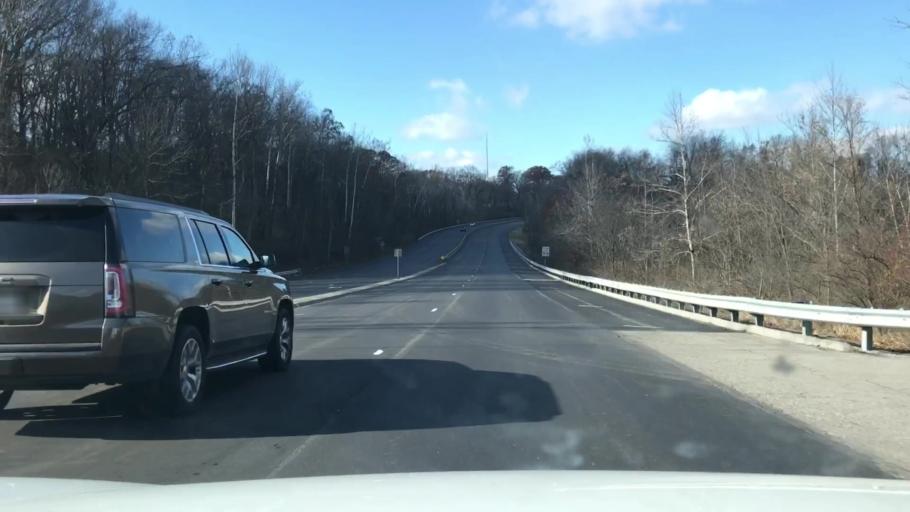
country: US
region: Illinois
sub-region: Saint Clair County
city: Fairview Heights
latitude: 38.5626
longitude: -90.0290
